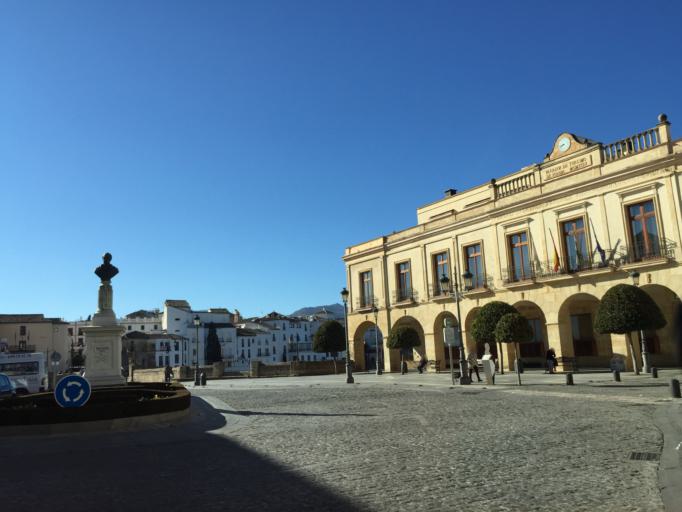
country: ES
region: Andalusia
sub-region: Provincia de Malaga
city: Ronda
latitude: 36.7415
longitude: -5.1662
